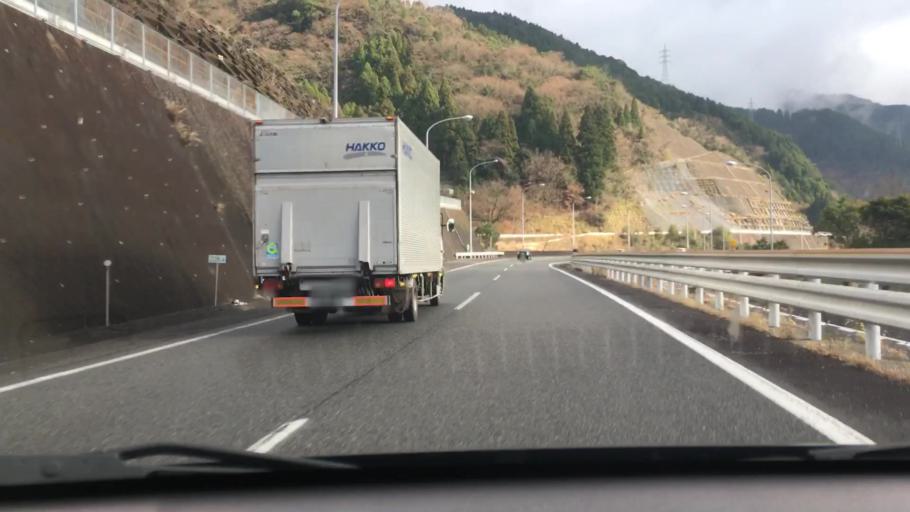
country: JP
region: Kumamoto
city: Yatsushiro
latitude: 32.4006
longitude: 130.7003
